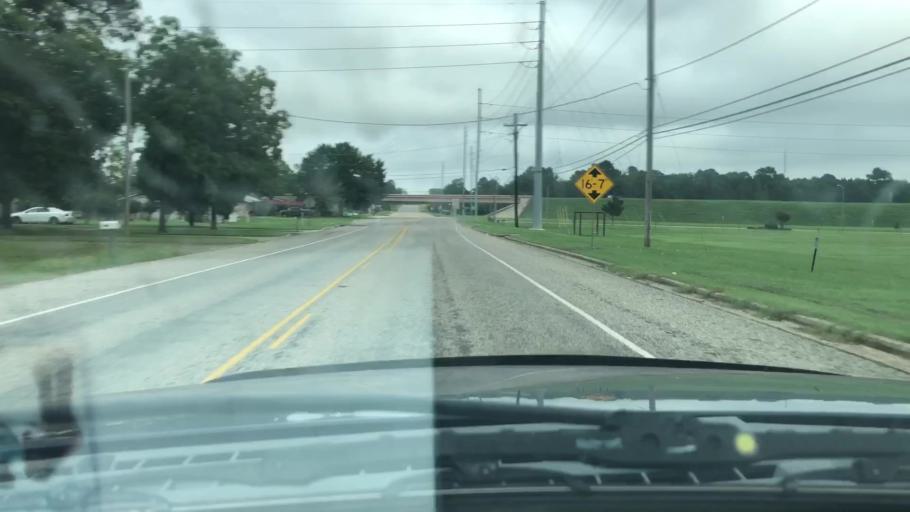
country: US
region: Texas
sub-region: Bowie County
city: Wake Village
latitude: 33.3837
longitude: -94.0921
